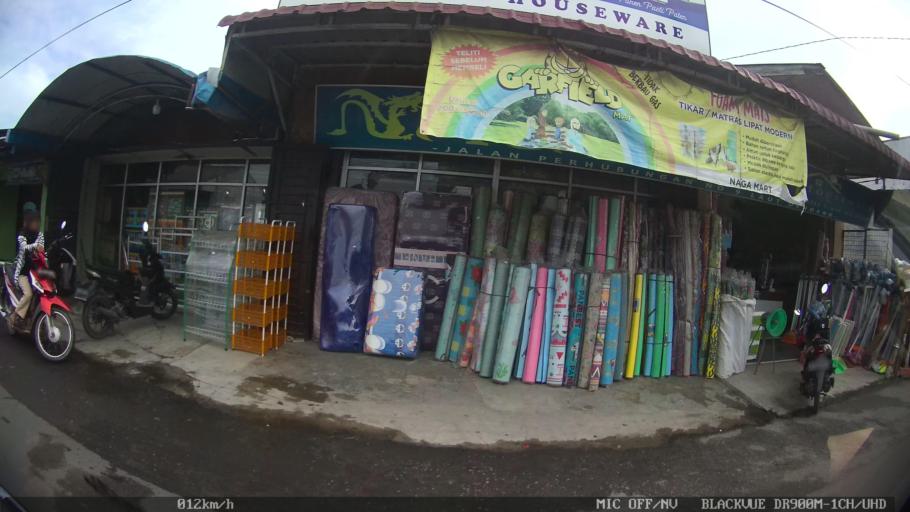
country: ID
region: North Sumatra
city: Medan
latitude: 3.6202
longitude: 98.7394
